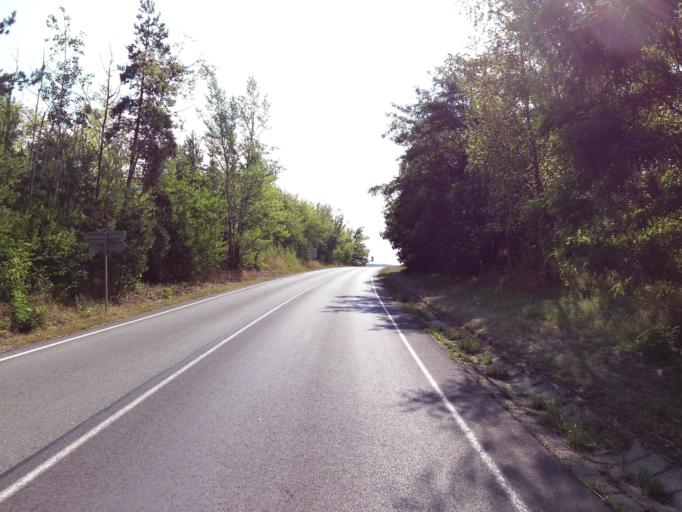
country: CZ
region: Central Bohemia
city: Mnichovo Hradiste
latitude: 50.5183
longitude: 14.9601
